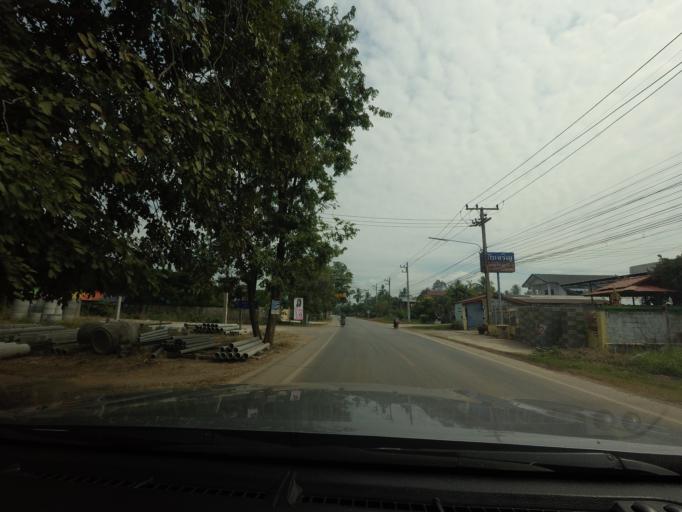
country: TH
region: Phitsanulok
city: Phitsanulok
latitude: 16.7244
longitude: 100.3132
